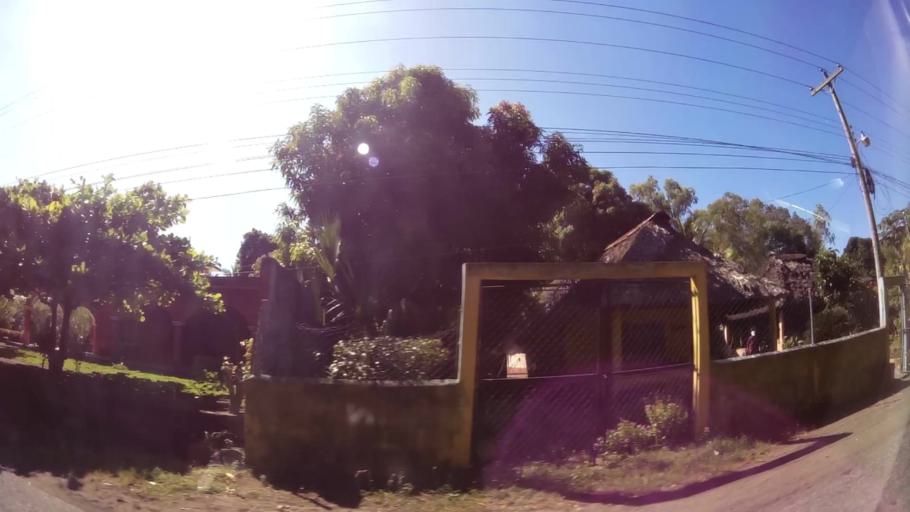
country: GT
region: Escuintla
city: Iztapa
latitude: 13.9211
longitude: -90.5669
